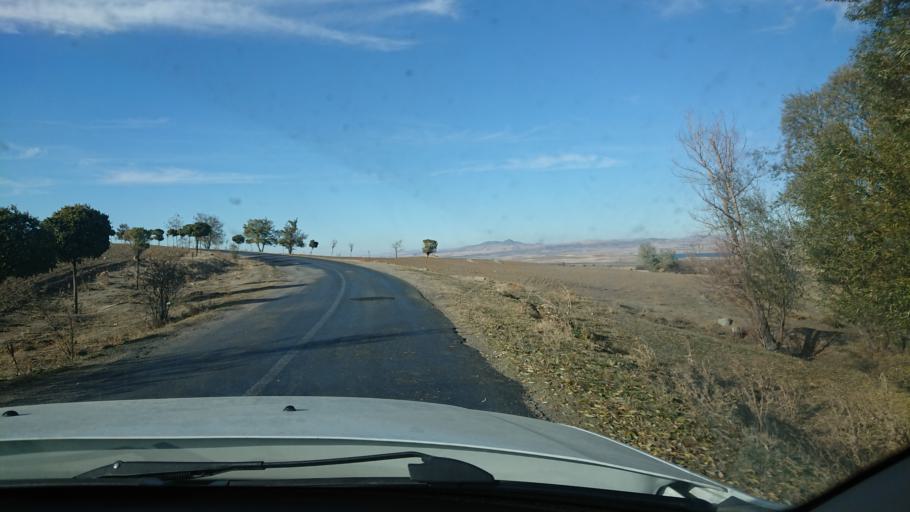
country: TR
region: Aksaray
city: Sariyahsi
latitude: 38.9706
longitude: 33.8663
